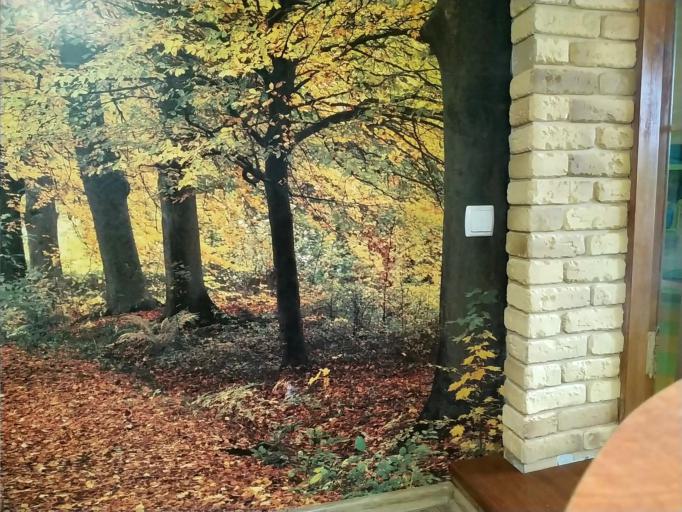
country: BY
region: Mogilev
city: Khotsimsk
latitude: 53.5535
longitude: 32.5209
